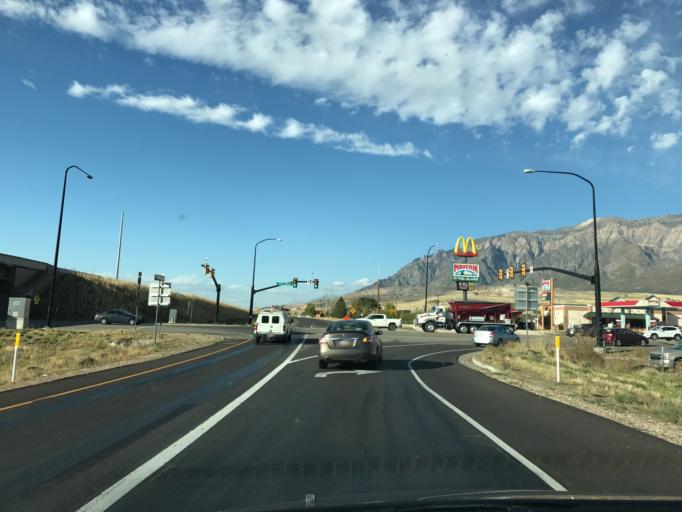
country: US
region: Utah
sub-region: Weber County
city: Farr West
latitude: 41.3057
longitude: -112.0253
